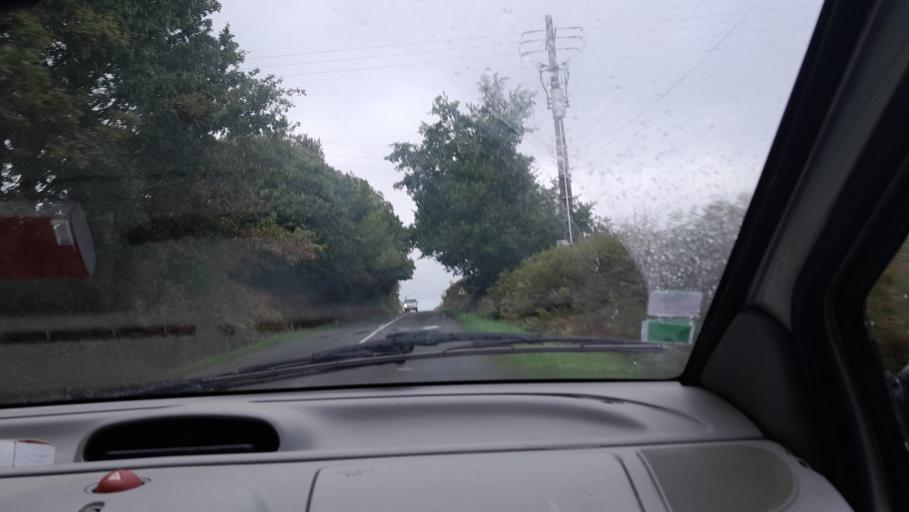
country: FR
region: Pays de la Loire
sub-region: Departement de la Mayenne
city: Congrier
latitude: 47.8658
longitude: -1.1313
